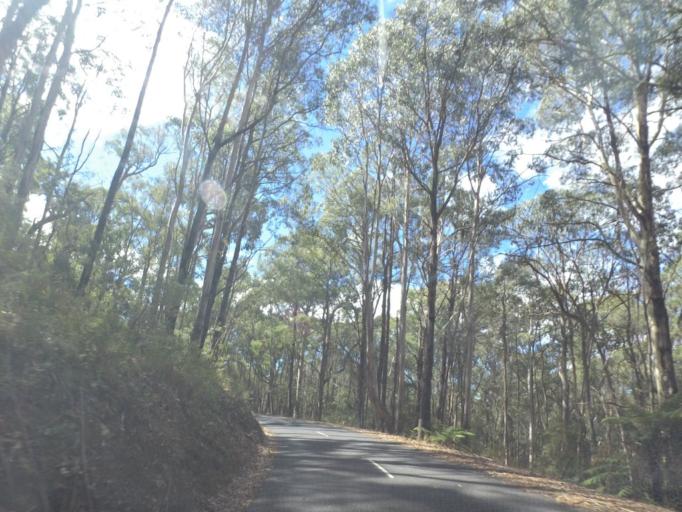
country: AU
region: Victoria
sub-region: Murrindindi
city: Alexandra
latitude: -37.3400
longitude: 145.9630
